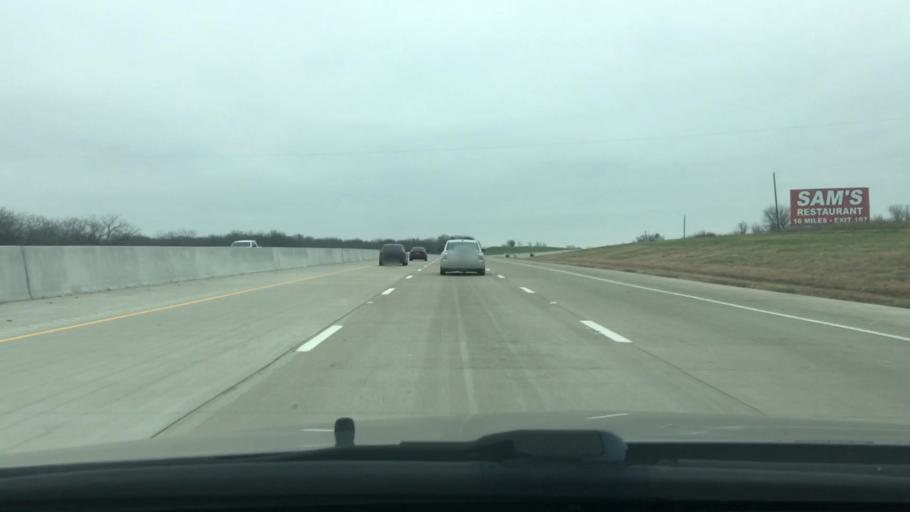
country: US
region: Texas
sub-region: Freestone County
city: Wortham
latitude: 31.8908
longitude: -96.3577
